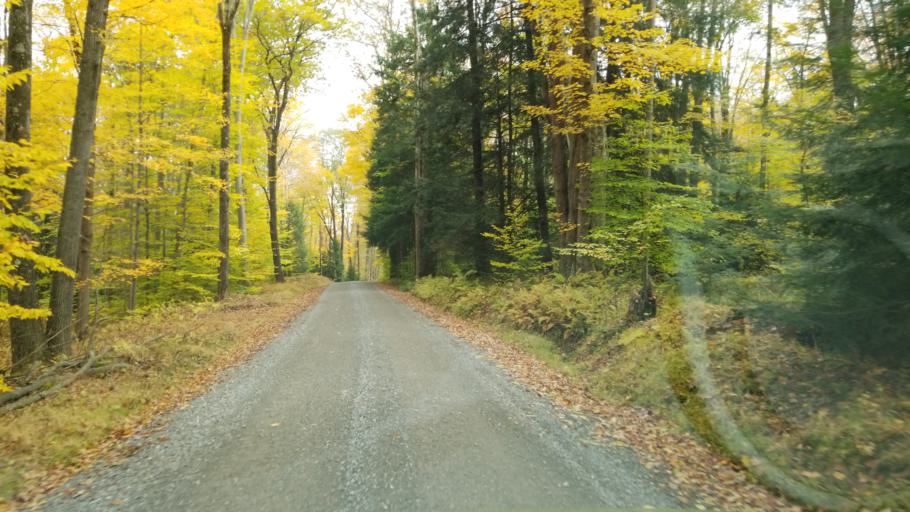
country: US
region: Pennsylvania
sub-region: Clearfield County
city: Clearfield
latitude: 41.1975
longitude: -78.4114
